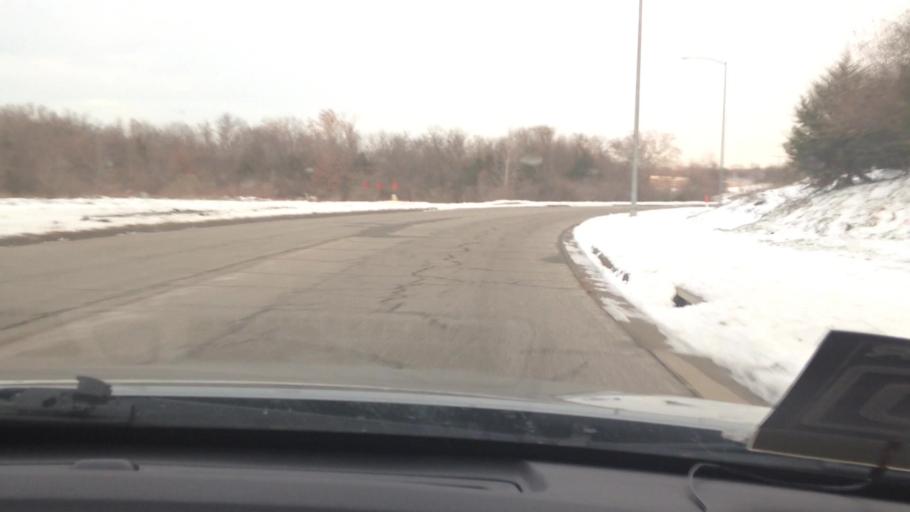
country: US
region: Kansas
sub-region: Leavenworth County
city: Lansing
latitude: 39.2463
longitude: -94.9141
